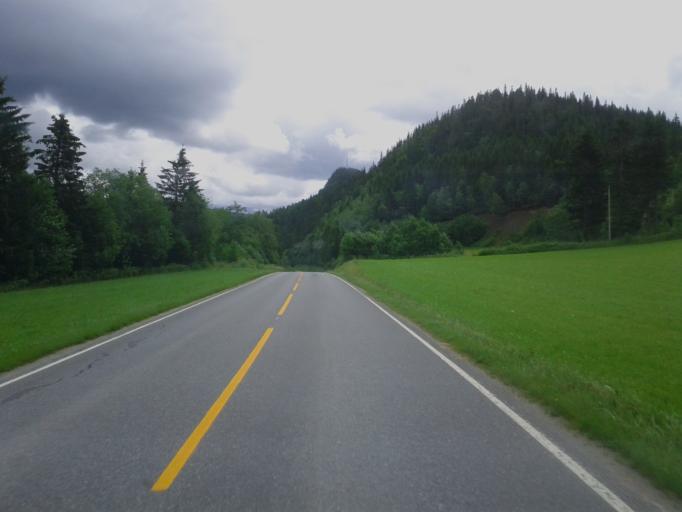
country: NO
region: Sor-Trondelag
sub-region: Midtre Gauldal
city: Storen
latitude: 62.9445
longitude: 10.6318
